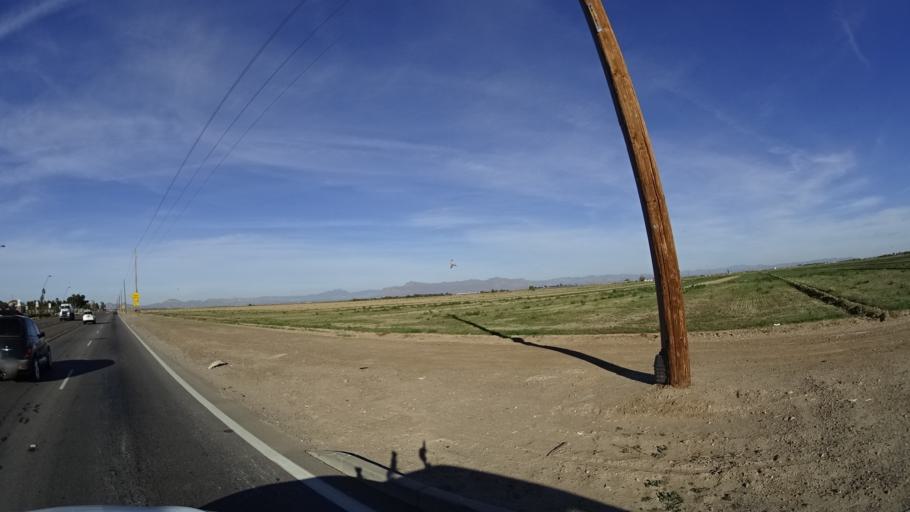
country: US
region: Arizona
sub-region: Maricopa County
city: Queen Creek
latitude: 33.2680
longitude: -111.6347
